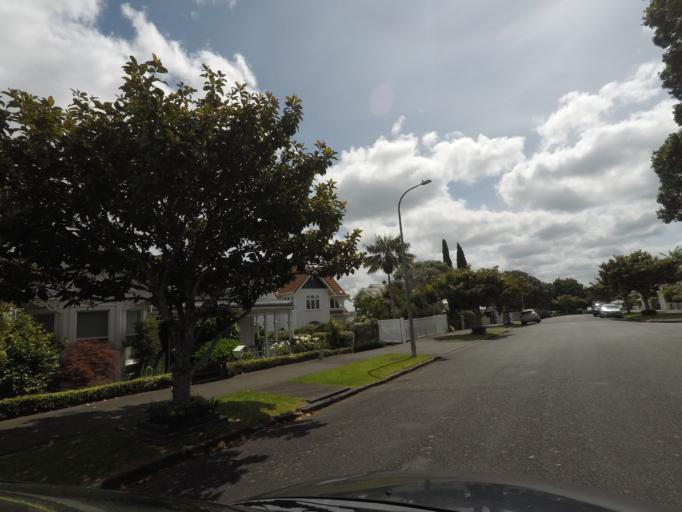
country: NZ
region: Auckland
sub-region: Auckland
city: Auckland
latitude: -36.8484
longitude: 174.7258
